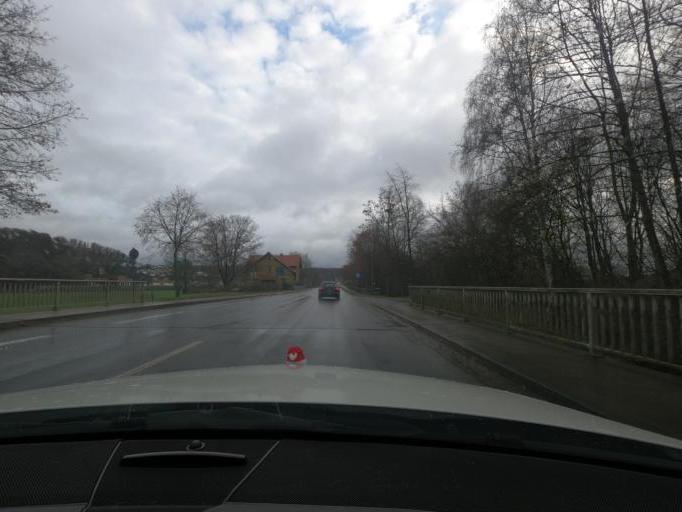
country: DE
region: Lower Saxony
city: Kreiensen
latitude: 51.8590
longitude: 9.9450
